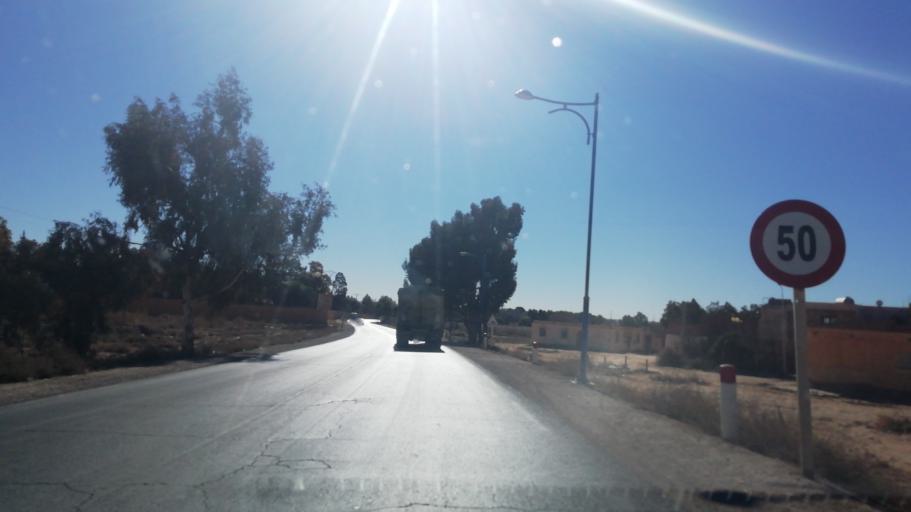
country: DZ
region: Saida
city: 'Ain el Hadjar
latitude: 34.1473
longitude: 0.0702
